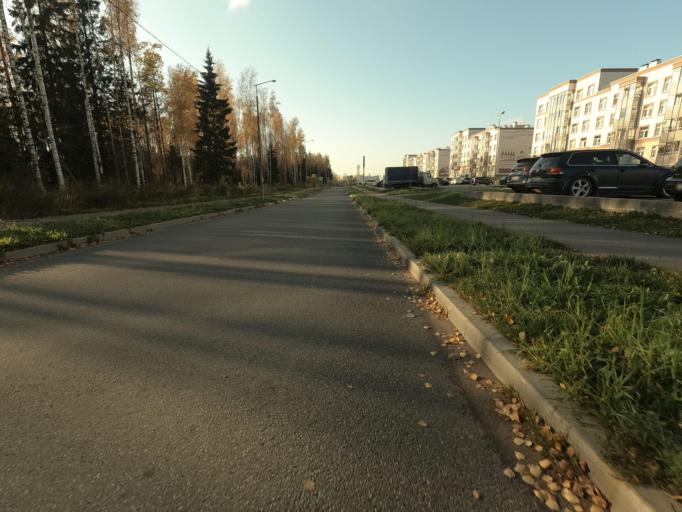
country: RU
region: Leningrad
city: Sertolovo
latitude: 60.1633
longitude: 30.1912
